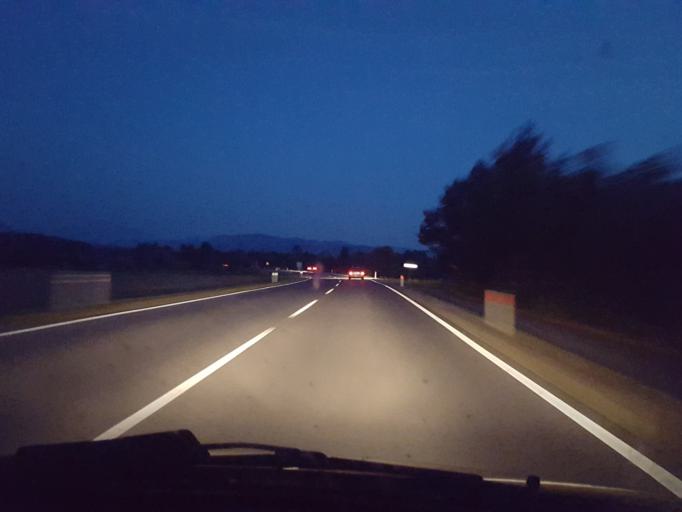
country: AT
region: Lower Austria
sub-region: Politischer Bezirk Scheibbs
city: Wieselburg
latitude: 48.0982
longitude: 15.1338
